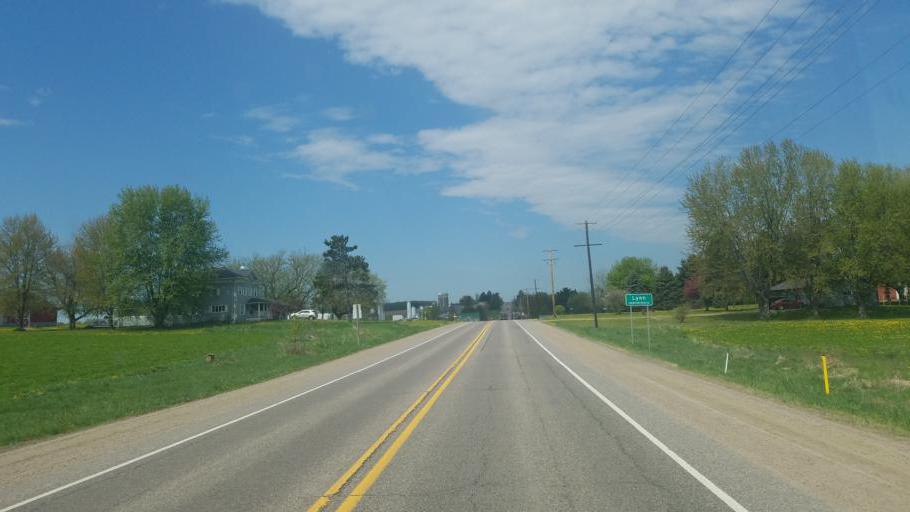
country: US
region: Wisconsin
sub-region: Clark County
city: Loyal
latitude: 44.5824
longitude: -90.3992
